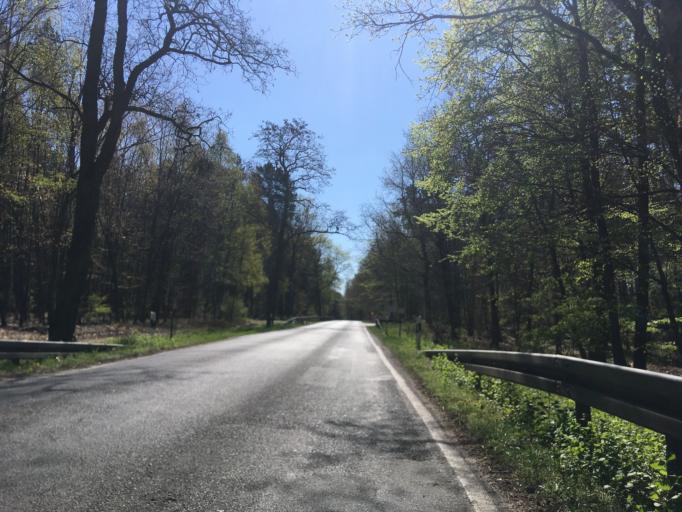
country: DE
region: Brandenburg
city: Bernau bei Berlin
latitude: 52.7154
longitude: 13.5757
